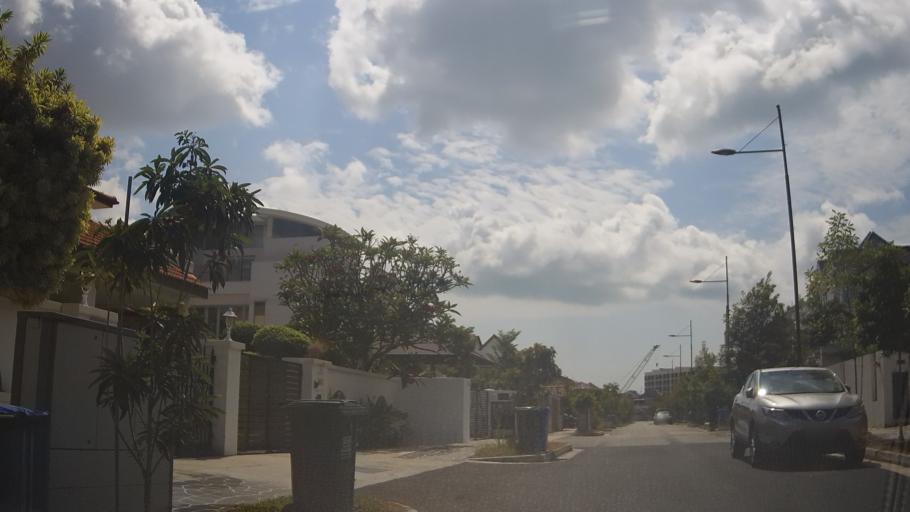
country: SG
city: Singapore
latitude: 1.3217
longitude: 103.9527
